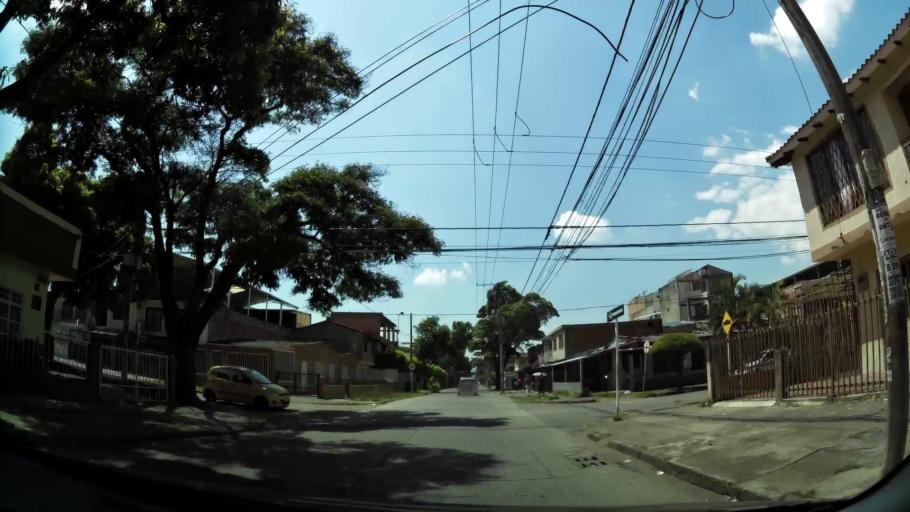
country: CO
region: Valle del Cauca
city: Cali
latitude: 3.4368
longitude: -76.5100
